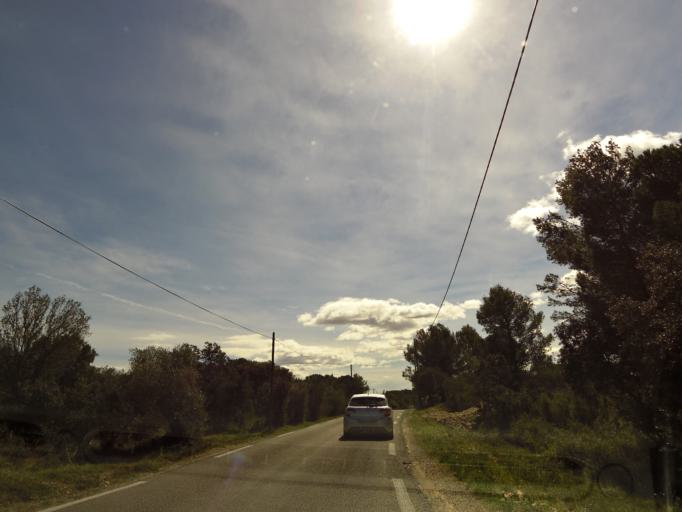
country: FR
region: Languedoc-Roussillon
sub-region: Departement du Gard
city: Bernis
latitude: 43.7848
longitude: 4.2689
